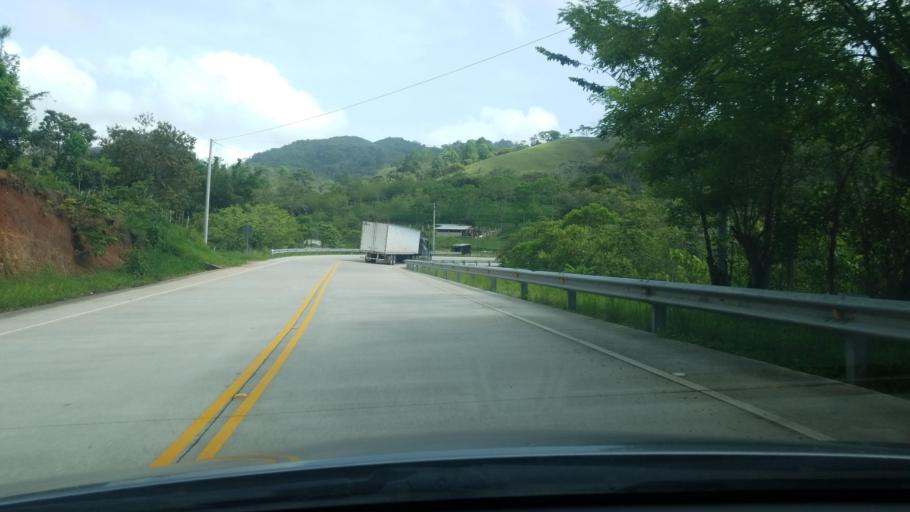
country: HN
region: Copan
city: San Jeronimo
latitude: 14.9452
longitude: -88.9144
